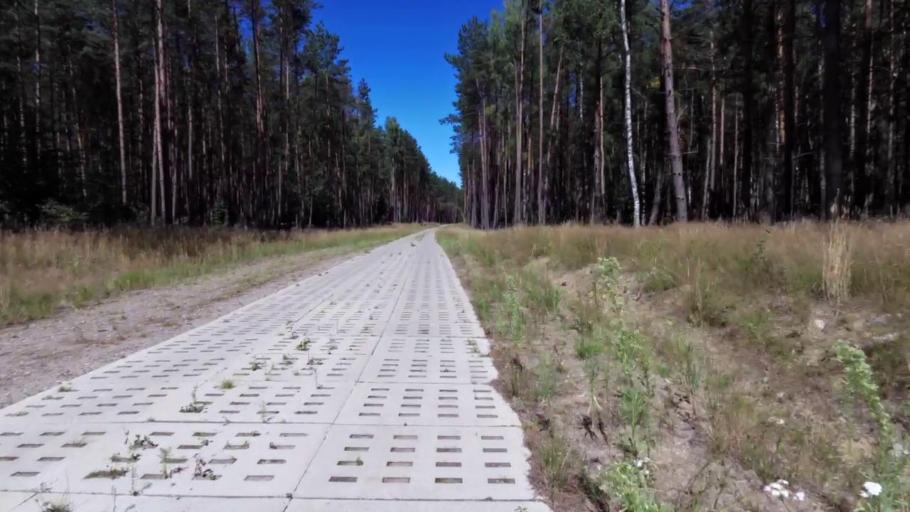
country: PL
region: West Pomeranian Voivodeship
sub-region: Powiat szczecinecki
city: Szczecinek
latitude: 53.6207
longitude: 16.6624
